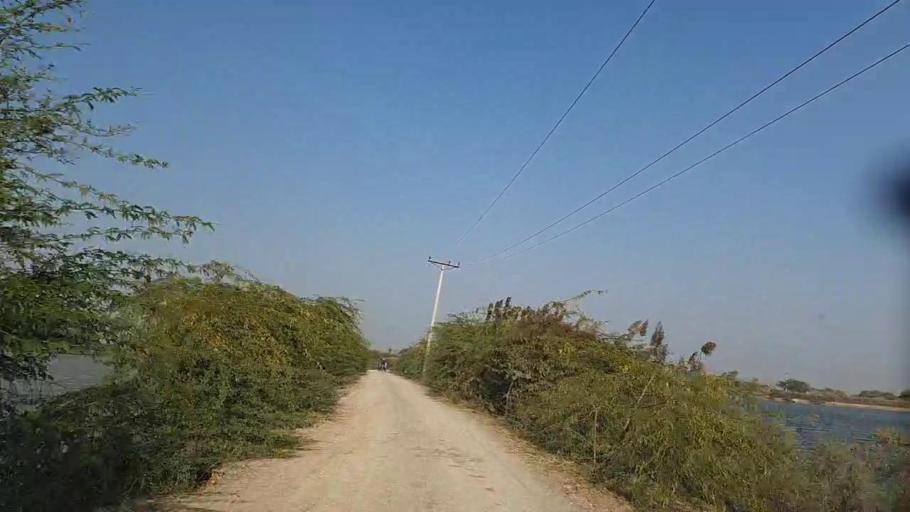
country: PK
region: Sindh
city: Jati
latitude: 24.5231
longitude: 68.2643
